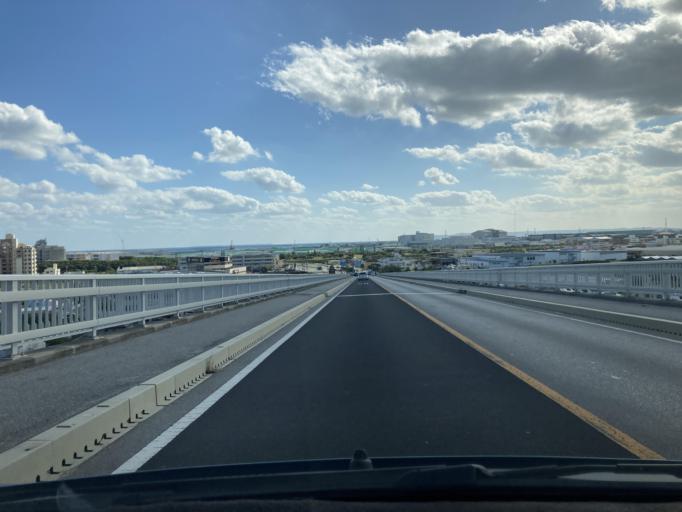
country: JP
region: Okinawa
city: Gushikawa
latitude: 26.3479
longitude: 127.8560
